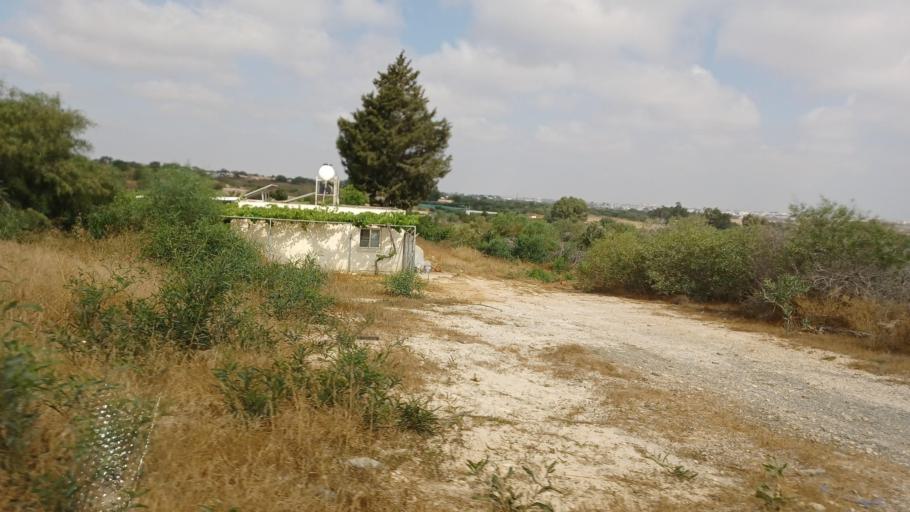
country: CY
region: Ammochostos
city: Ayia Napa
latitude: 35.0102
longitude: 34.0085
